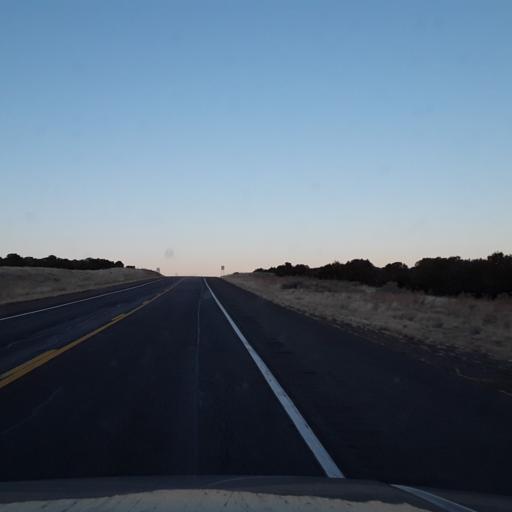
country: US
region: New Mexico
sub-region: Guadalupe County
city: Santa Rosa
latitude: 34.5299
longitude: -105.3215
